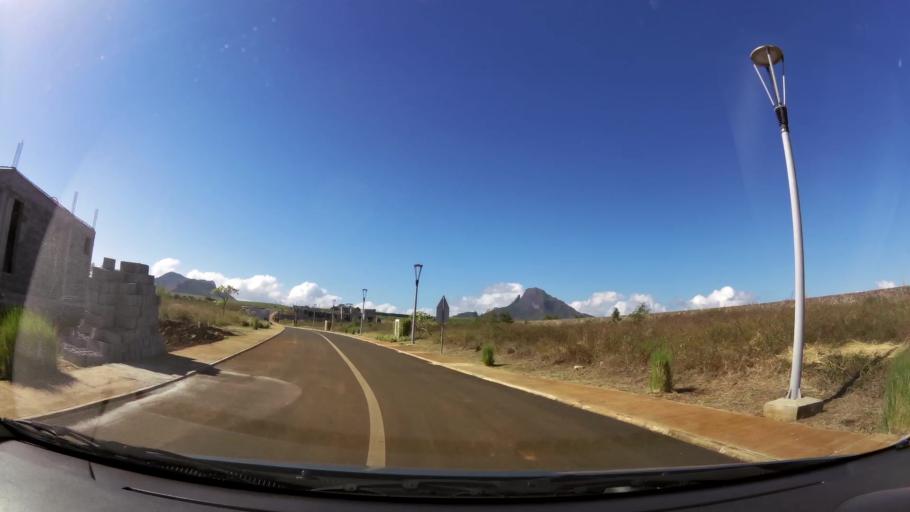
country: MU
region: Black River
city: Flic en Flac
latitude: -20.2708
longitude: 57.3824
